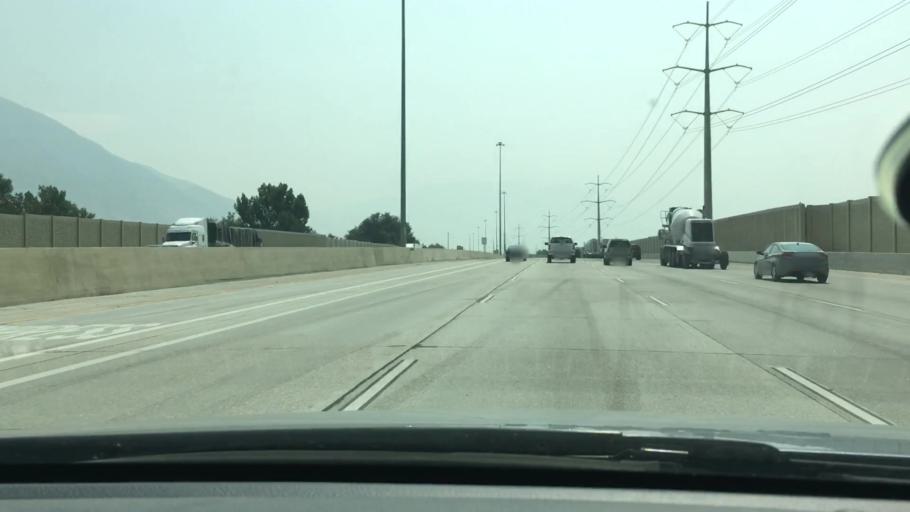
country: US
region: Utah
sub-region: Utah County
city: Provo
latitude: 40.2264
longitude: -111.6777
